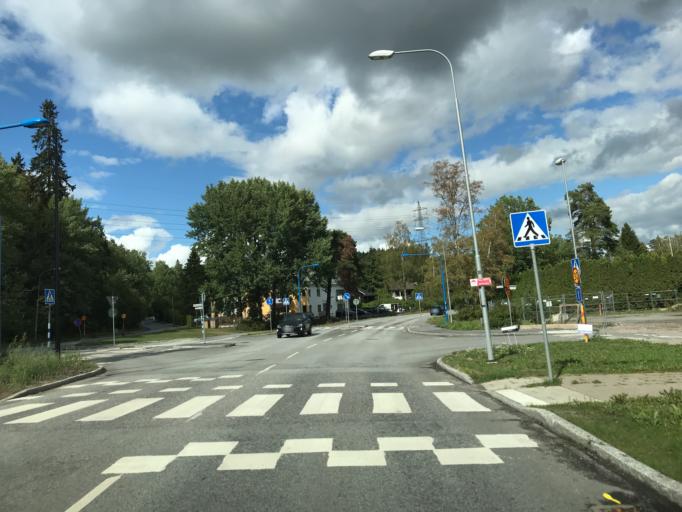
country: SE
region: Stockholm
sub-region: Sollentuna Kommun
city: Sollentuna
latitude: 59.4486
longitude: 17.9510
